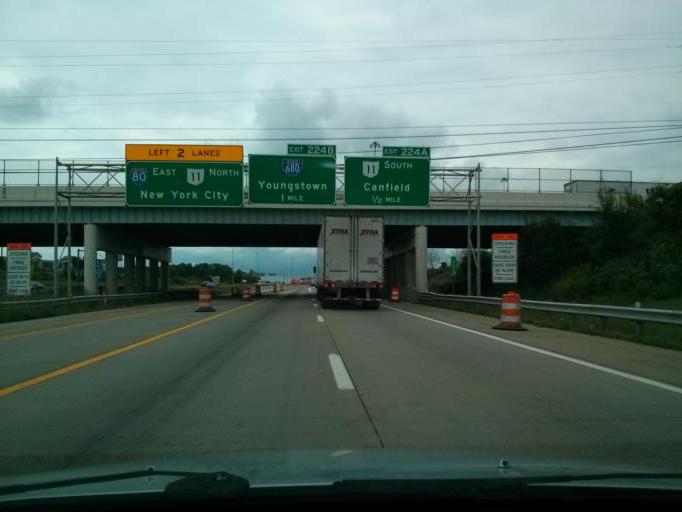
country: US
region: Ohio
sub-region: Trumbull County
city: Mineral Ridge
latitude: 41.1237
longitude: -80.7690
